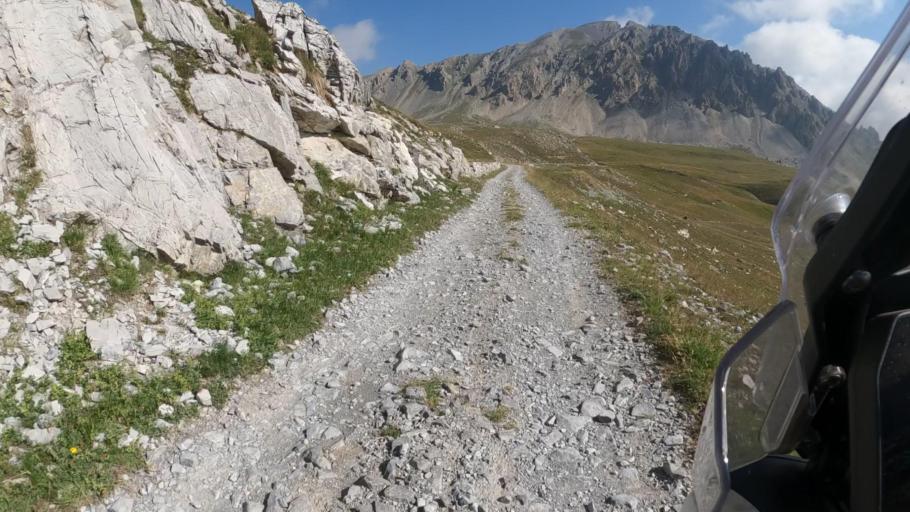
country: IT
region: Piedmont
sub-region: Provincia di Cuneo
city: Bersezio
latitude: 44.4024
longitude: 7.0158
